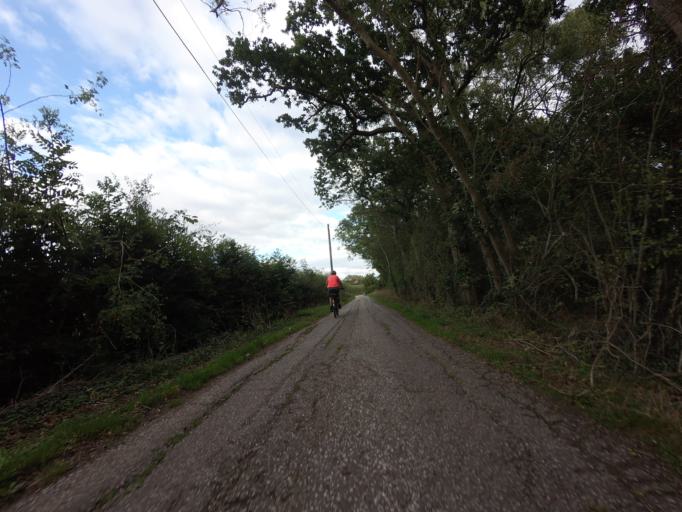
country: GB
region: England
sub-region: Kent
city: Staplehurst
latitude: 51.2116
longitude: 0.5493
